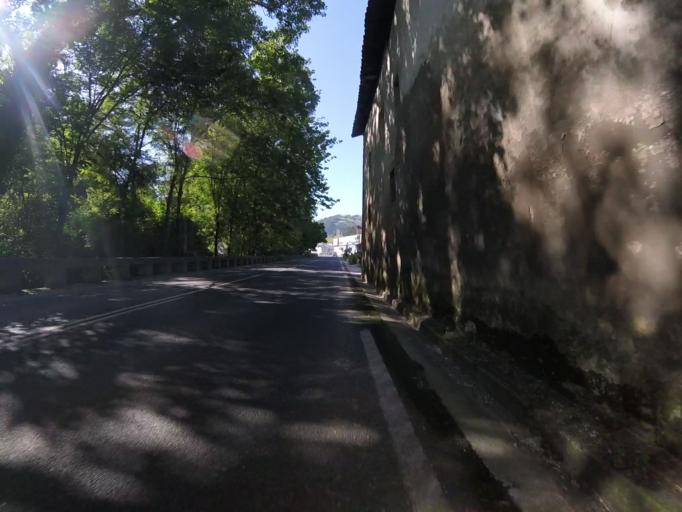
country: ES
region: Basque Country
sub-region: Provincia de Guipuzcoa
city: Azpeitia
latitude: 43.1666
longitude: -2.2493
